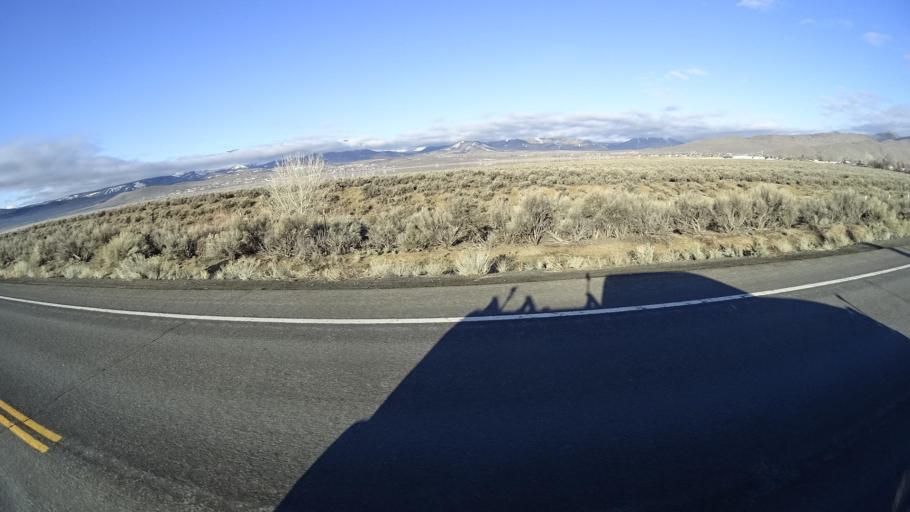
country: US
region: Nevada
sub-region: Washoe County
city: Cold Springs
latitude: 39.6666
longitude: -119.9605
